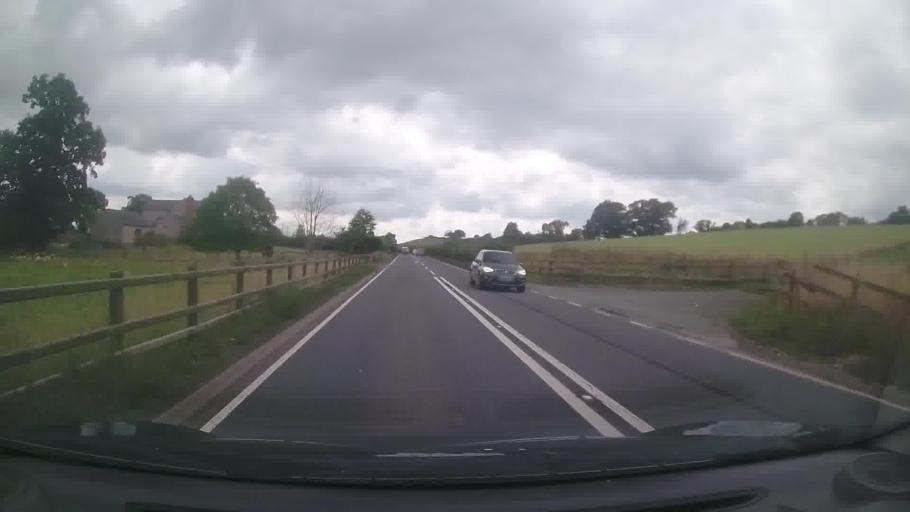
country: GB
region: England
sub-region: Shropshire
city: Oswestry
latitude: 52.8242
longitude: -3.0573
